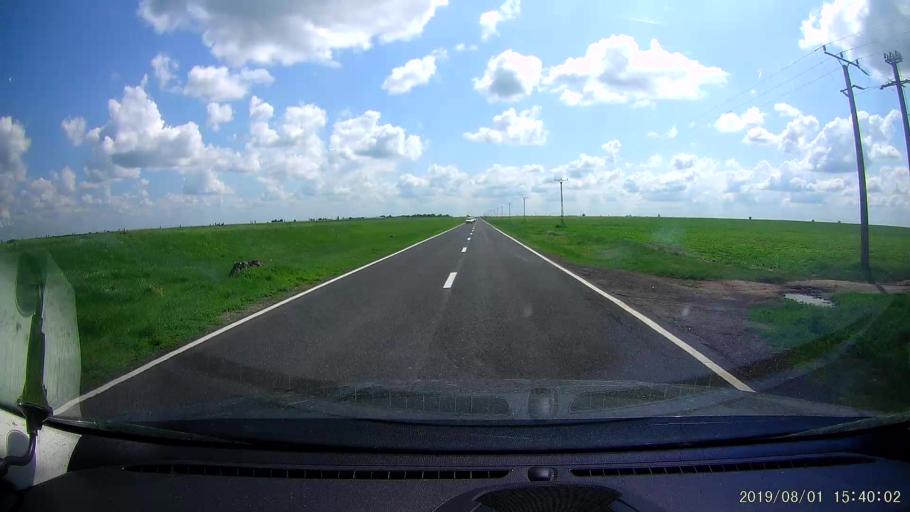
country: RO
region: Braila
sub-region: Comuna Baraganul
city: Baraganul
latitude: 44.8451
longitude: 27.5491
